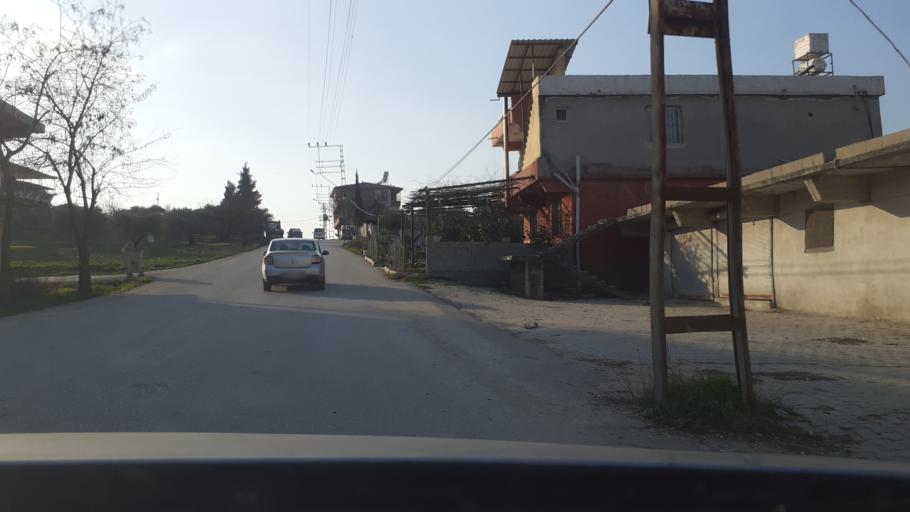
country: TR
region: Hatay
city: Oymakli
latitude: 36.1136
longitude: 36.2902
